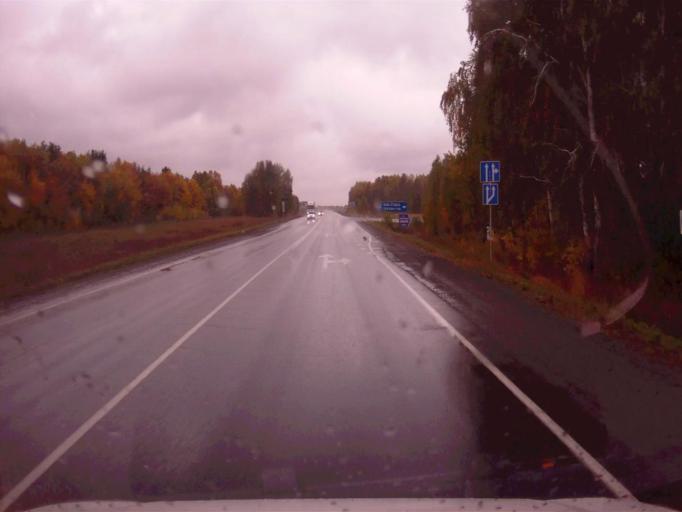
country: RU
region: Chelyabinsk
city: Roshchino
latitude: 55.3951
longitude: 61.0997
